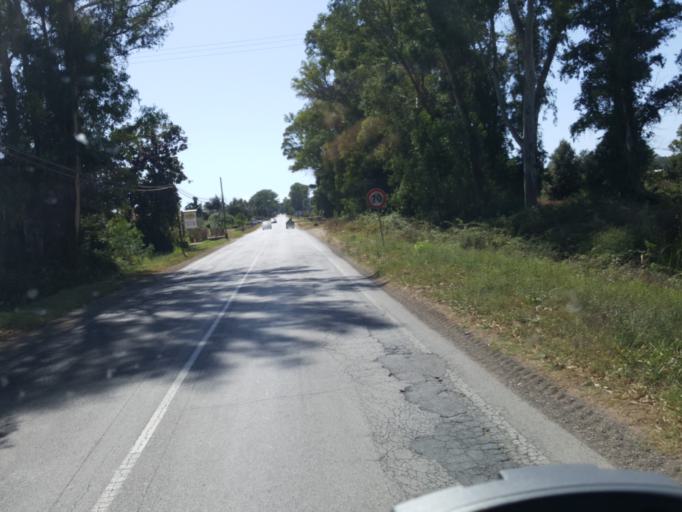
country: IT
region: Latium
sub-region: Provincia di Latina
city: Sabaudia
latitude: 41.3449
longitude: 13.0895
